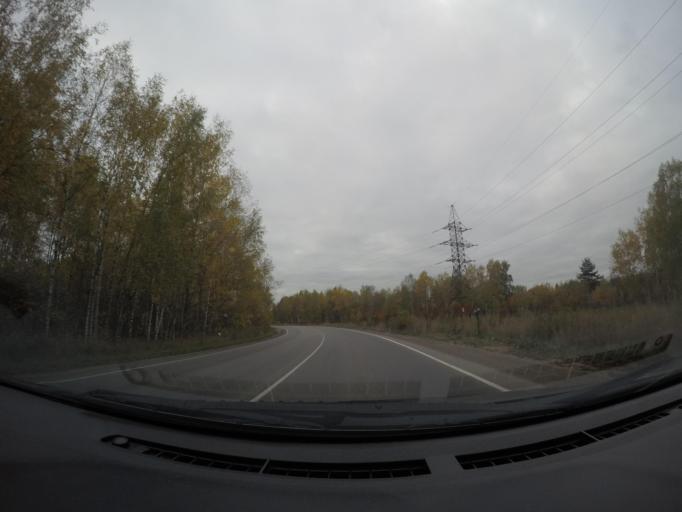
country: RU
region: Moskovskaya
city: Imeni Vorovskogo
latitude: 55.7531
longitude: 38.2660
